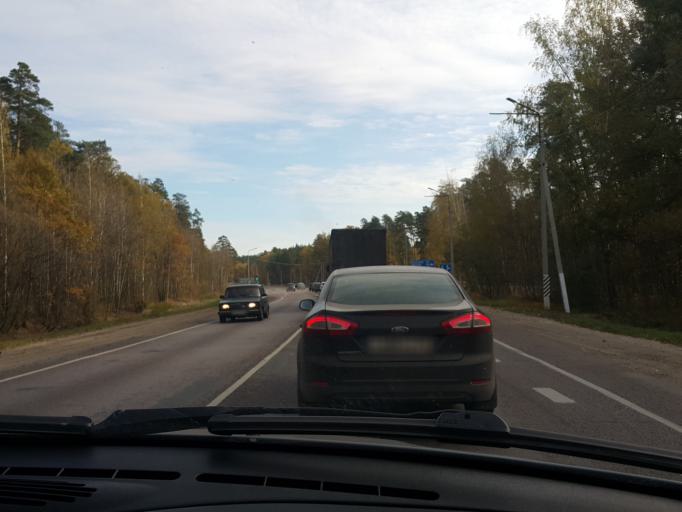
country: RU
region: Tambov
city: Donskoye
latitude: 52.7068
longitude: 41.5427
